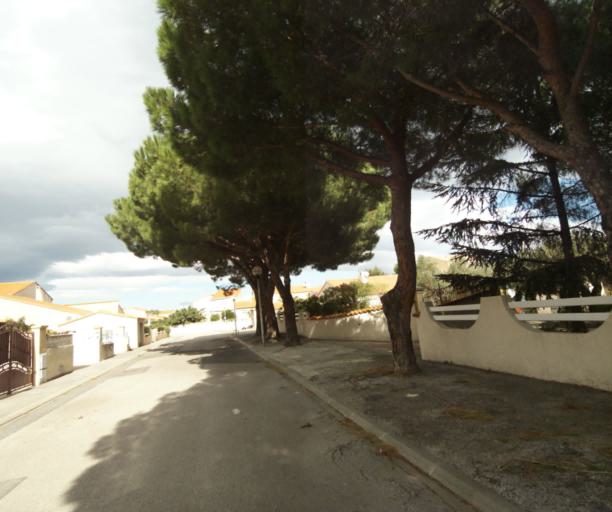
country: FR
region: Languedoc-Roussillon
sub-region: Departement des Pyrenees-Orientales
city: Argelers
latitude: 42.5516
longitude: 3.0185
